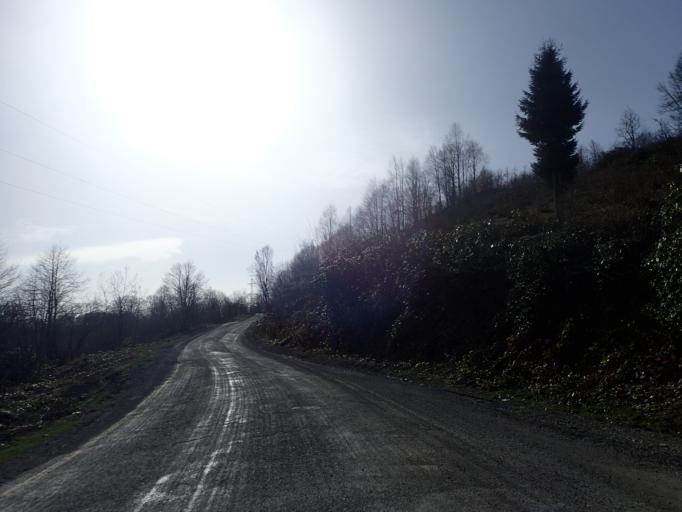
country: TR
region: Ordu
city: Kabaduz
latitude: 40.7771
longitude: 37.9257
